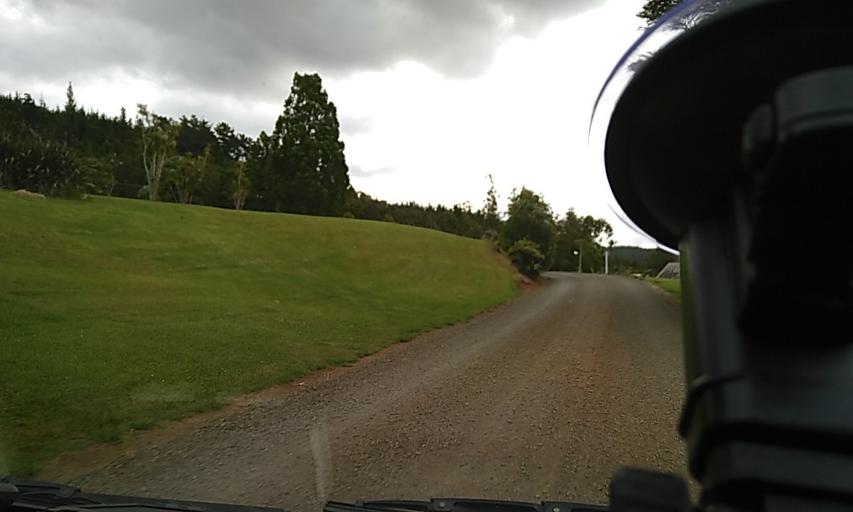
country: NZ
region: Northland
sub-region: Kaipara District
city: Dargaville
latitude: -35.6525
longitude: 173.5570
